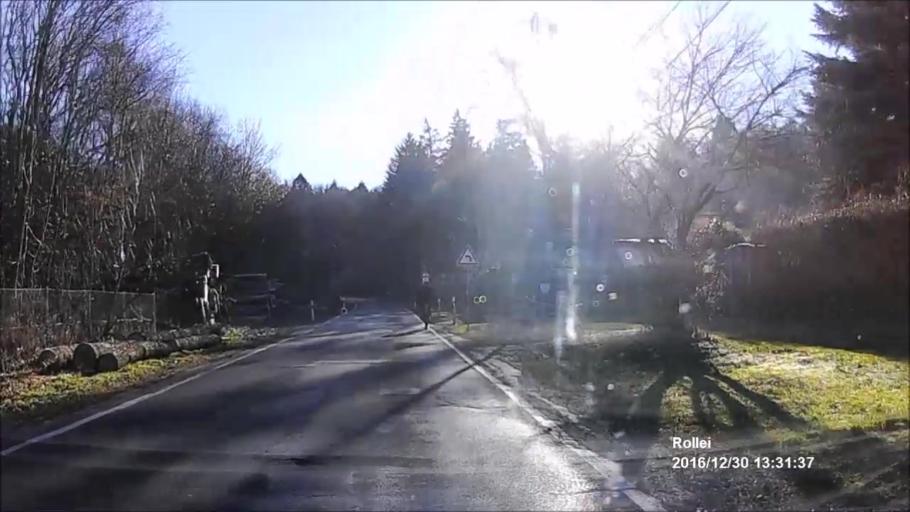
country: DE
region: Thuringia
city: Klettbach
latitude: 50.9339
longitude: 11.1031
